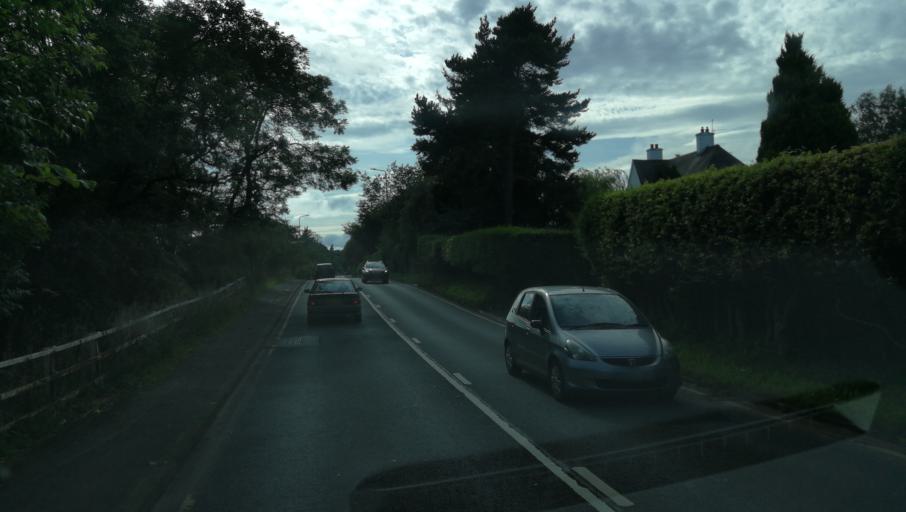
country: GB
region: Scotland
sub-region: Edinburgh
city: Balerno
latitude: 55.8909
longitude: -3.3270
